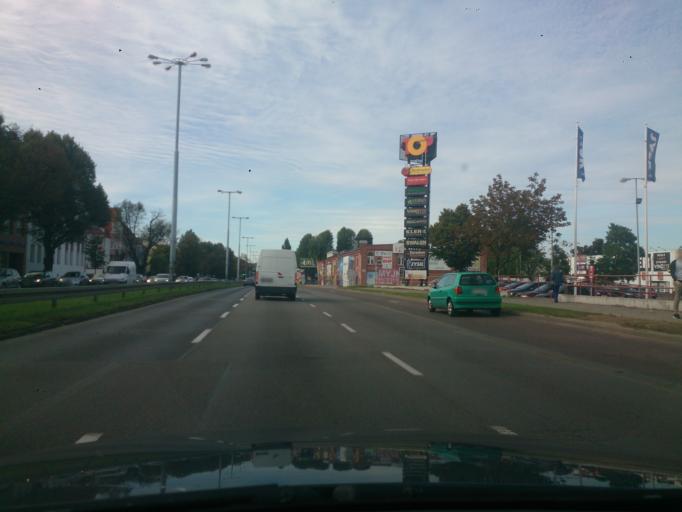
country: PL
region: Pomeranian Voivodeship
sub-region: Sopot
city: Sopot
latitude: 54.3880
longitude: 18.5905
